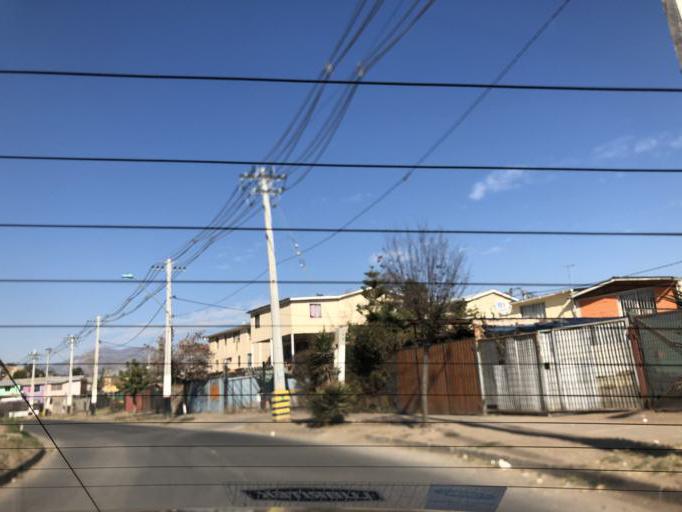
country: CL
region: Santiago Metropolitan
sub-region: Provincia de Cordillera
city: Puente Alto
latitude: -33.6234
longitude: -70.6055
